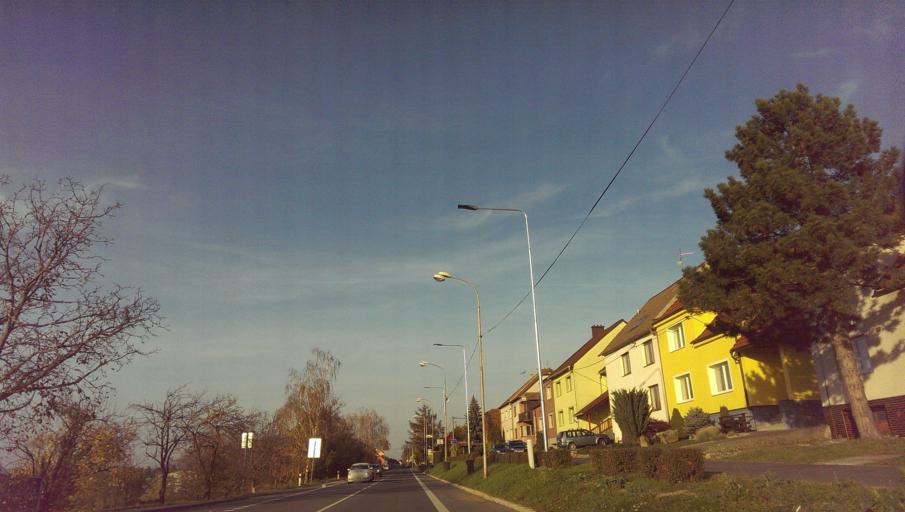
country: CZ
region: Zlin
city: Kunovice
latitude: 49.0328
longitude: 17.4600
